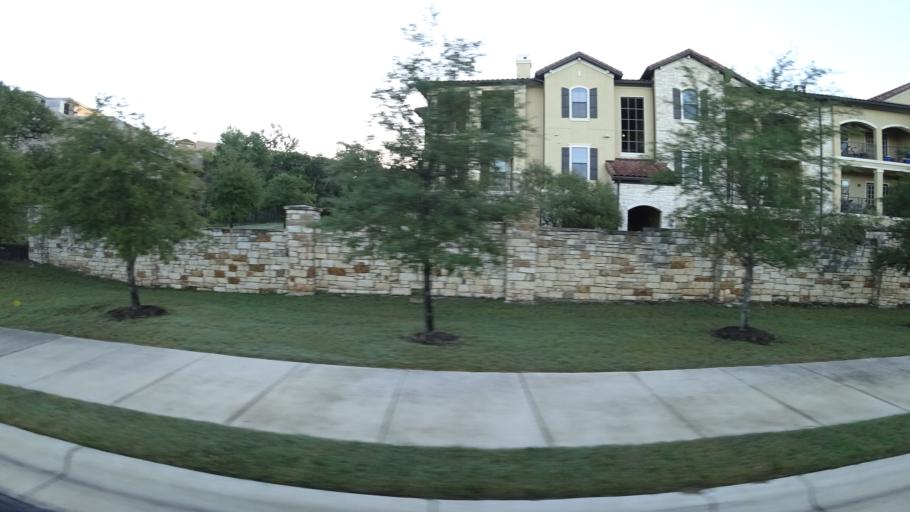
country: US
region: Texas
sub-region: Travis County
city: West Lake Hills
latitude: 30.3342
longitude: -97.8101
